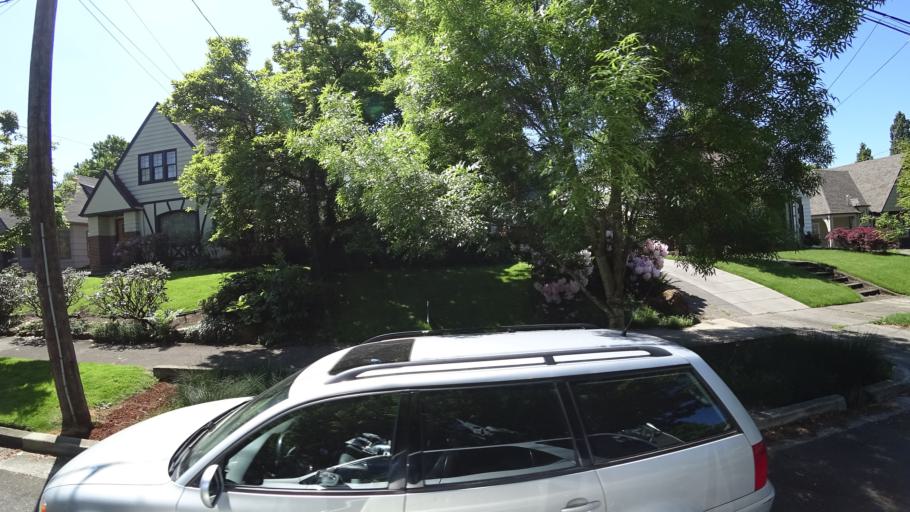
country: US
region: Oregon
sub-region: Multnomah County
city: Portland
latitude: 45.5105
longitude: -122.6390
